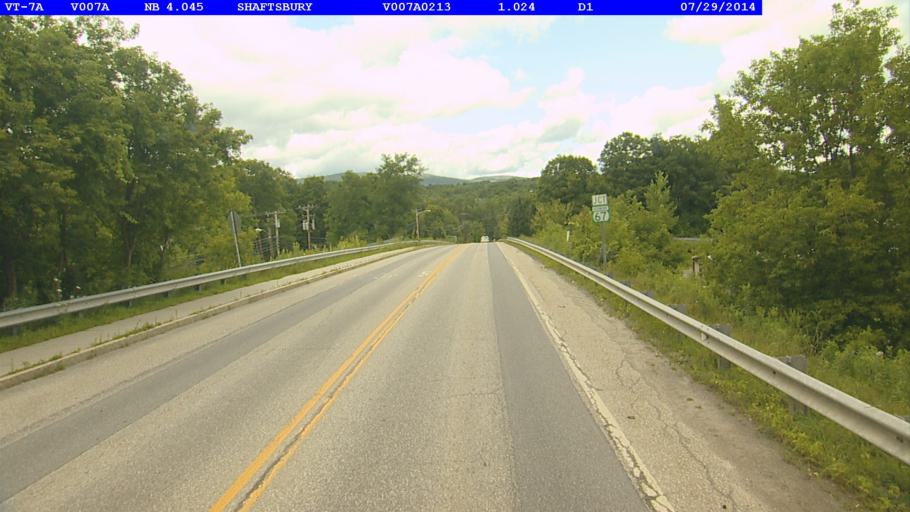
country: US
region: Vermont
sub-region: Bennington County
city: North Bennington
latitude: 42.9473
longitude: -73.2112
